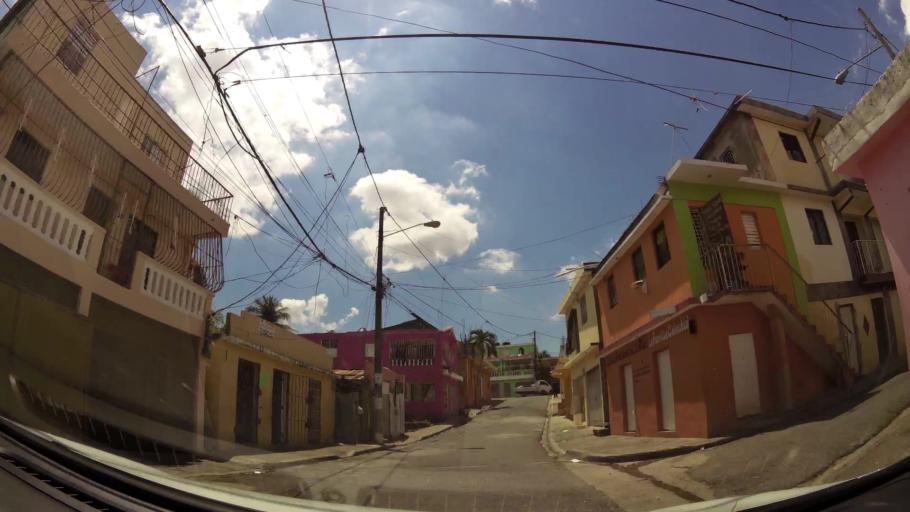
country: DO
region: Santo Domingo
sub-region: Santo Domingo
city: Santo Domingo Este
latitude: 18.5405
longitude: -69.8604
